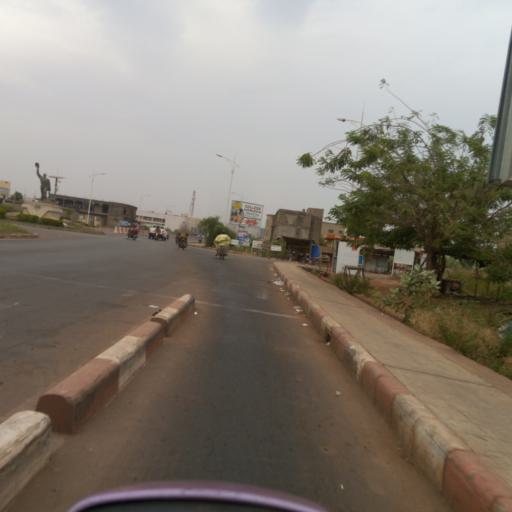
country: ML
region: Bamako
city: Bamako
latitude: 12.6558
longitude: -7.9317
